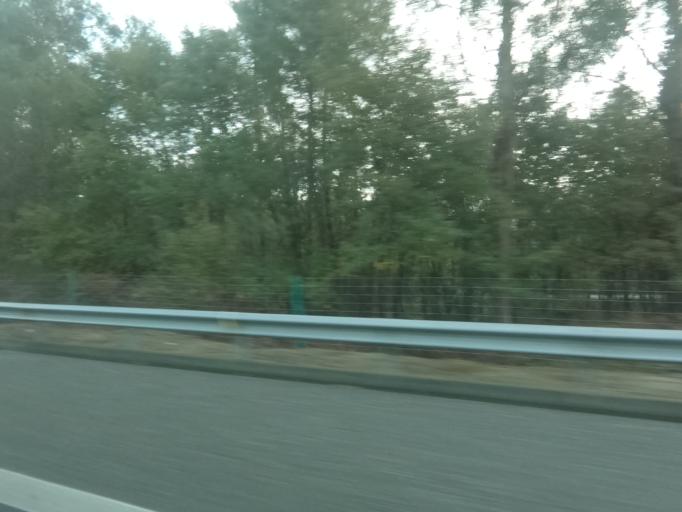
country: ES
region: Galicia
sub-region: Provincia de Pontevedra
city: Tui
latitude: 42.0795
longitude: -8.6397
